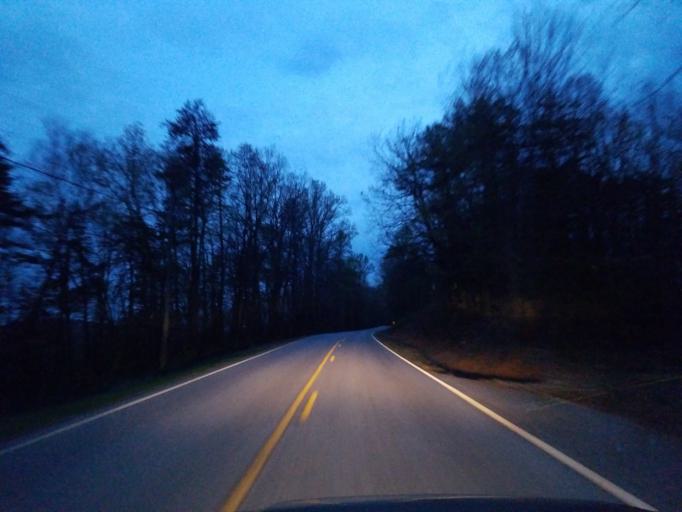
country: US
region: Georgia
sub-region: Lumpkin County
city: Dahlonega
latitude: 34.6212
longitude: -83.9594
